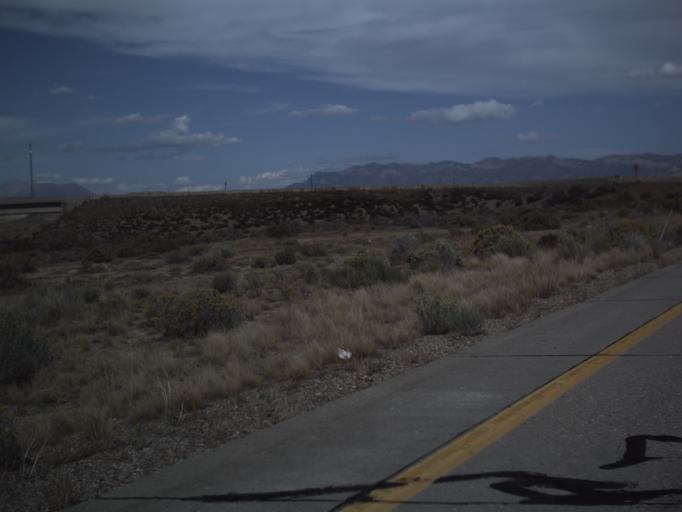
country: US
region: Utah
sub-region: Juab County
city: Nephi
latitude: 39.4336
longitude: -112.0339
